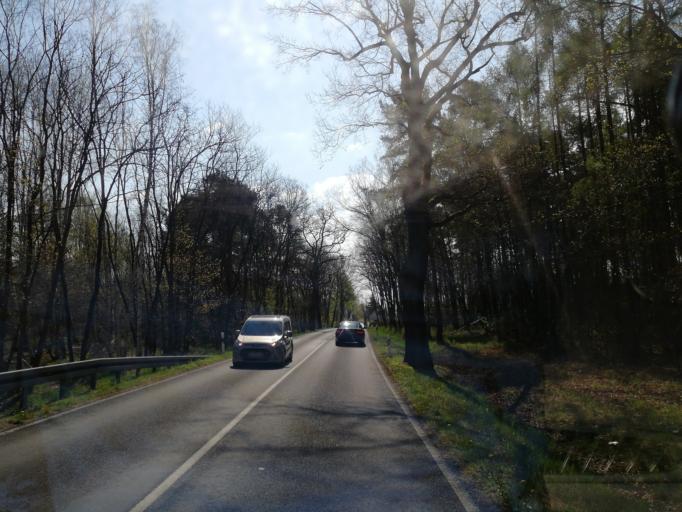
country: DE
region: Brandenburg
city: Calau
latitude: 51.7719
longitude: 13.8983
